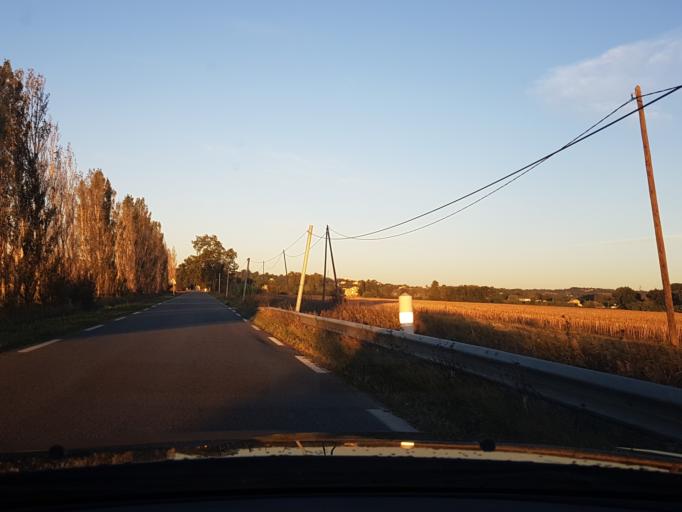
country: FR
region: Provence-Alpes-Cote d'Azur
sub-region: Departement du Vaucluse
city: Bedarrides
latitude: 44.0334
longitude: 4.9197
